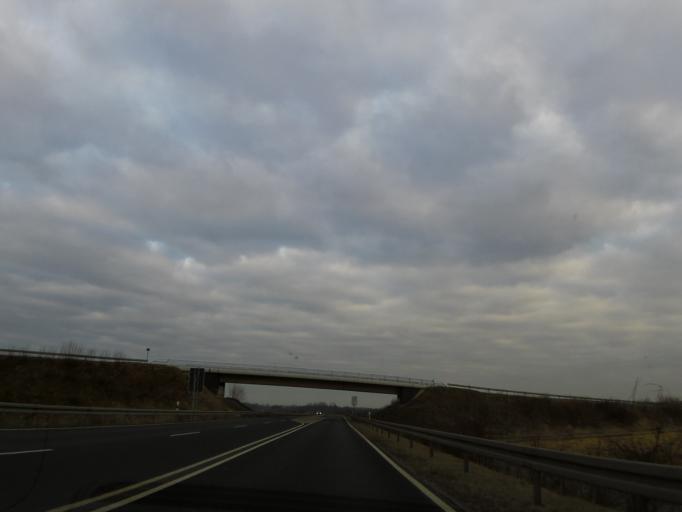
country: DE
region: North Rhine-Westphalia
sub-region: Regierungsbezirk Koln
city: Selfkant
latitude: 51.0271
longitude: 5.8975
